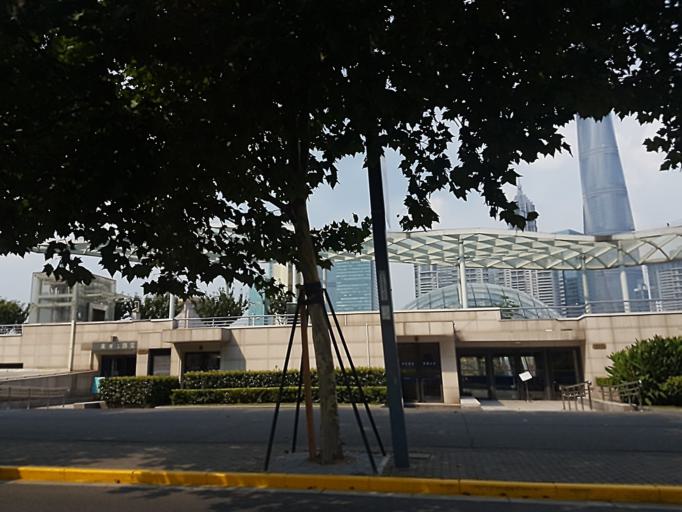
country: CN
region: Shanghai Shi
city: Hongkou
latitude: 31.2310
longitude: 121.4920
